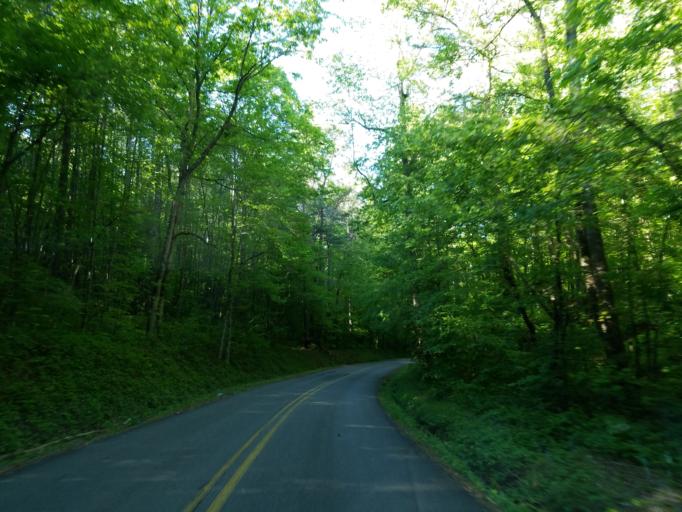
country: US
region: Georgia
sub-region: Gilmer County
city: Ellijay
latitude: 34.5700
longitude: -84.5167
